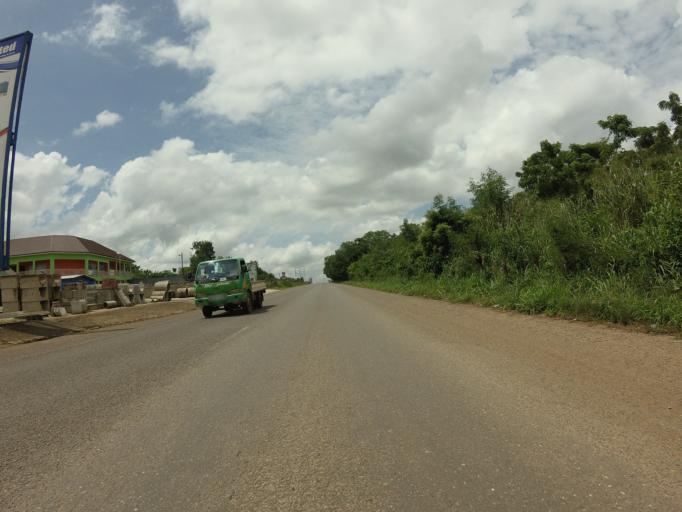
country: GH
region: Eastern
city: Aburi
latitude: 5.8279
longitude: -0.1187
